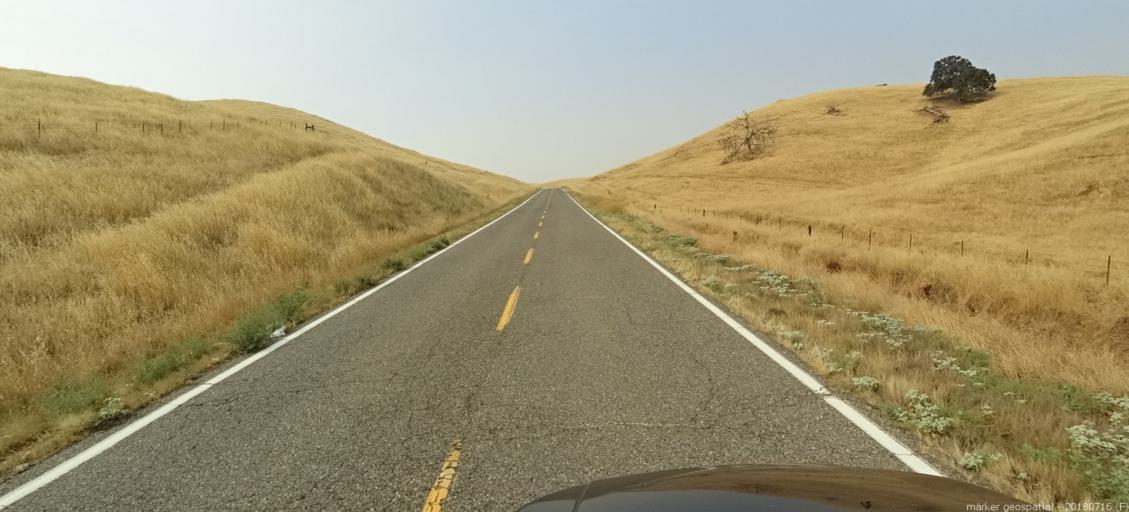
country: US
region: California
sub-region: Madera County
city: Madera Acres
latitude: 37.1944
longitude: -120.0032
